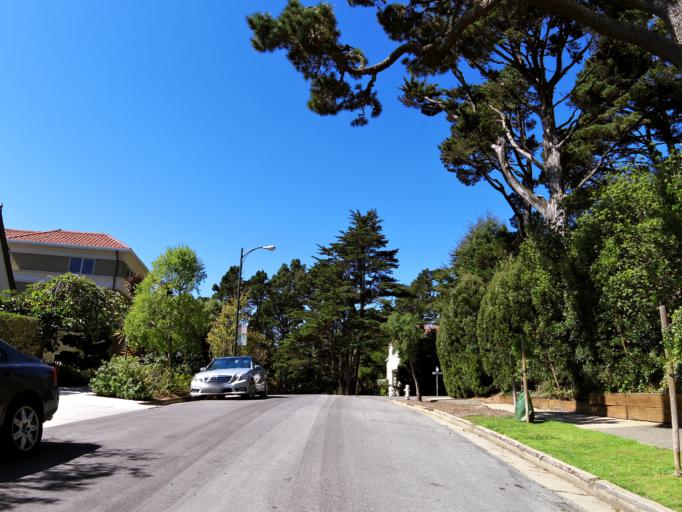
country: US
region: California
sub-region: San Mateo County
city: Daly City
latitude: 37.7467
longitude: -122.4632
